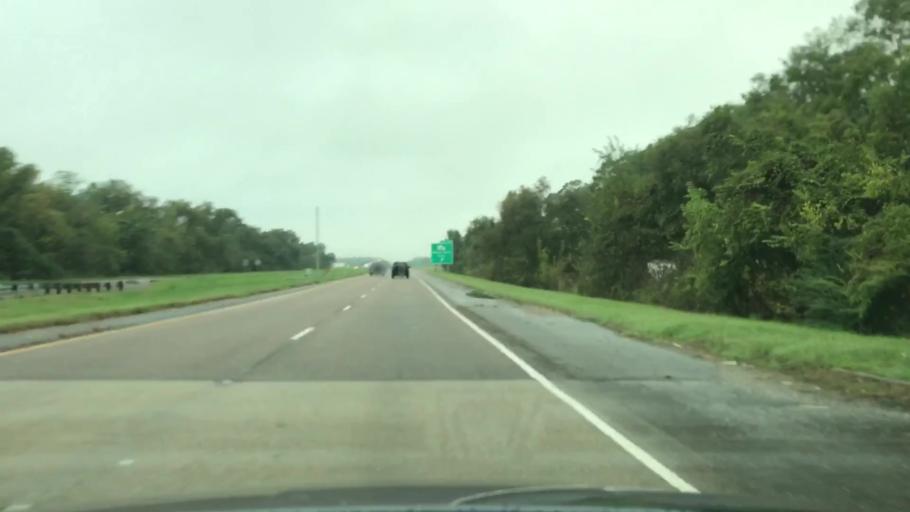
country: US
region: Louisiana
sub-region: Terrebonne Parish
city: Gray
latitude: 29.6838
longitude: -90.7406
